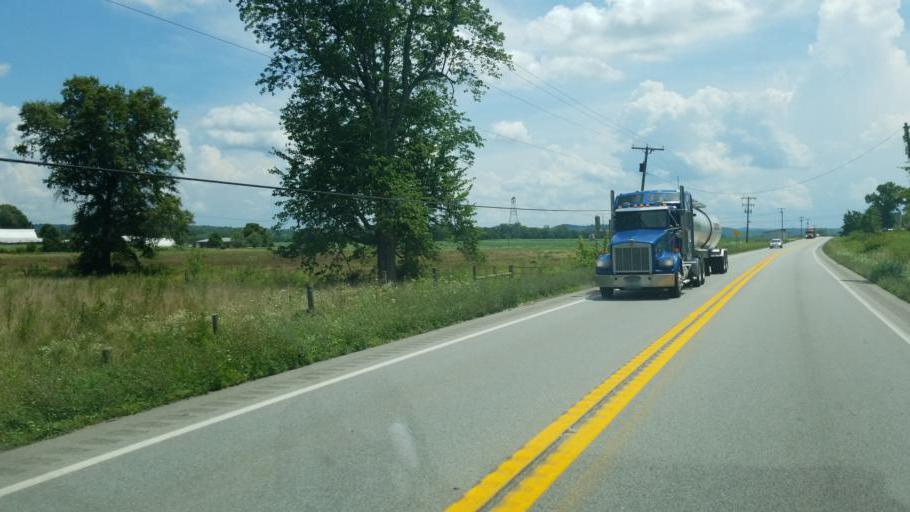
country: US
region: West Virginia
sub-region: Putnam County
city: Buffalo
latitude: 38.7508
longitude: -81.9853
